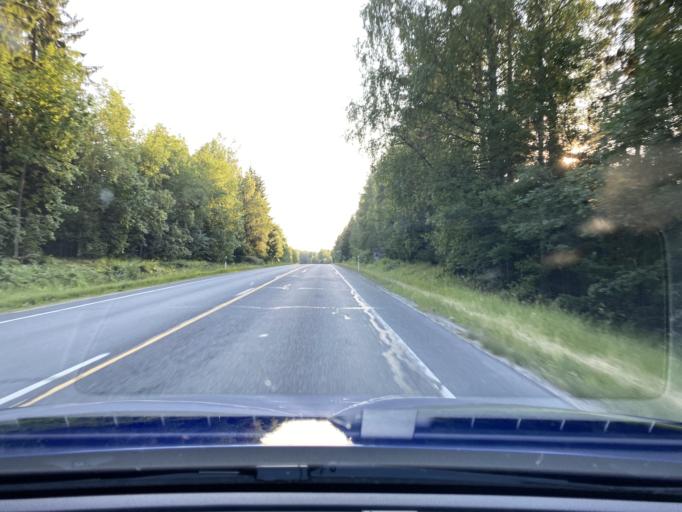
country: FI
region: Haeme
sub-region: Forssa
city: Tammela
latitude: 60.8268
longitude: 23.9353
